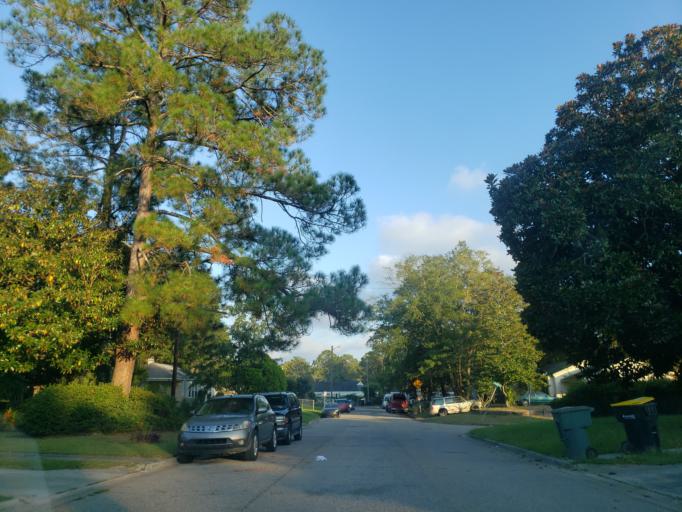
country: US
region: Georgia
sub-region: Chatham County
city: Thunderbolt
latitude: 32.0520
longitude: -81.0737
